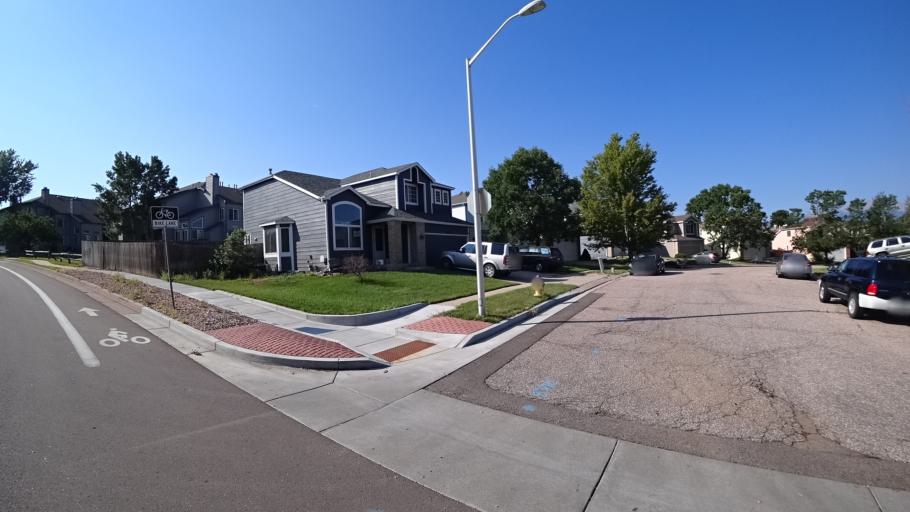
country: US
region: Colorado
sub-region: El Paso County
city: Air Force Academy
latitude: 38.9467
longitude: -104.7764
